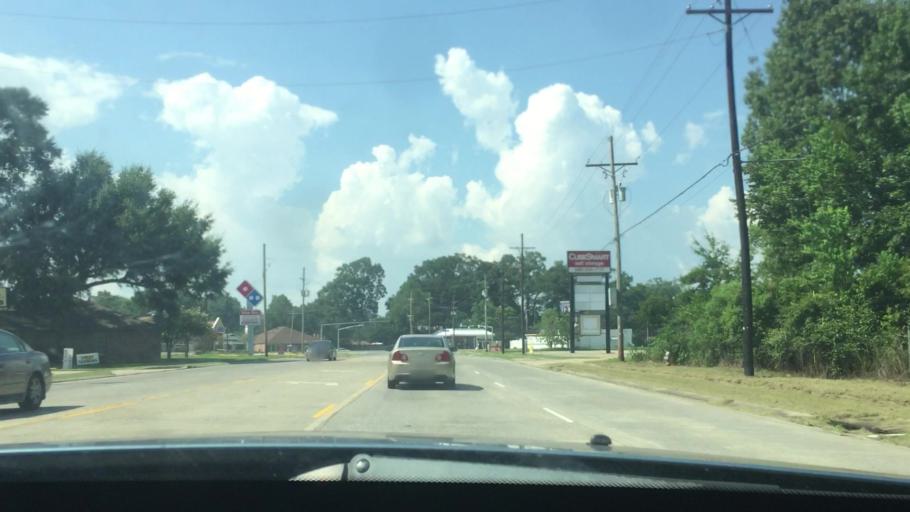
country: US
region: Louisiana
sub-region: East Baton Rouge Parish
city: Monticello
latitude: 30.4497
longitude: -91.0245
